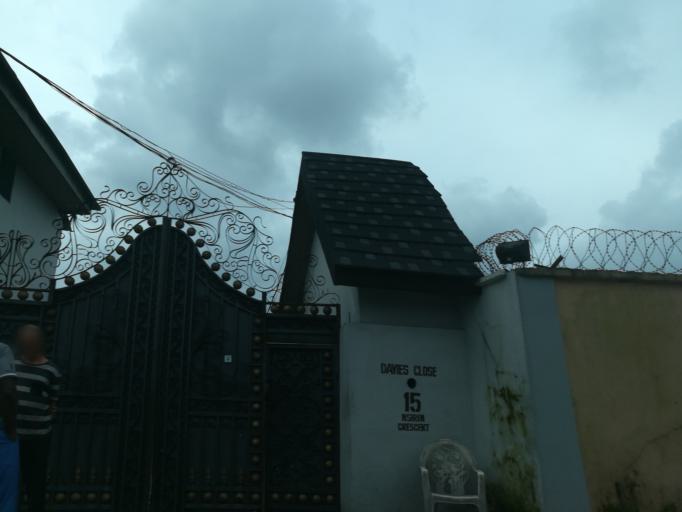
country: NG
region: Rivers
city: Port Harcourt
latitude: 4.8122
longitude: 6.9916
